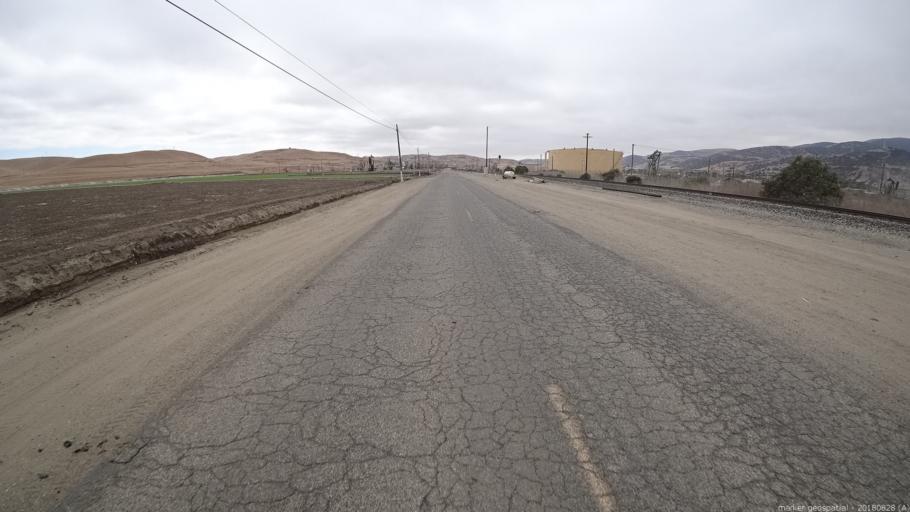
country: US
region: California
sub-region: San Luis Obispo County
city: Lake Nacimiento
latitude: 35.9692
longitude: -120.8724
